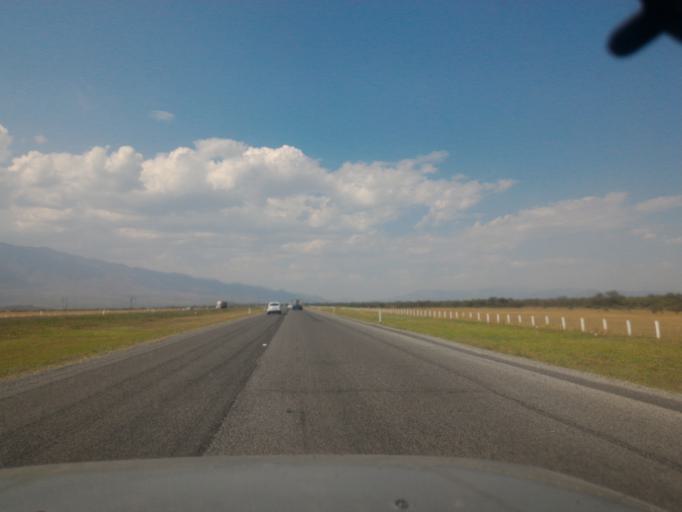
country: MX
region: Jalisco
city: Atoyac
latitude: 19.9675
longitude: -103.5342
